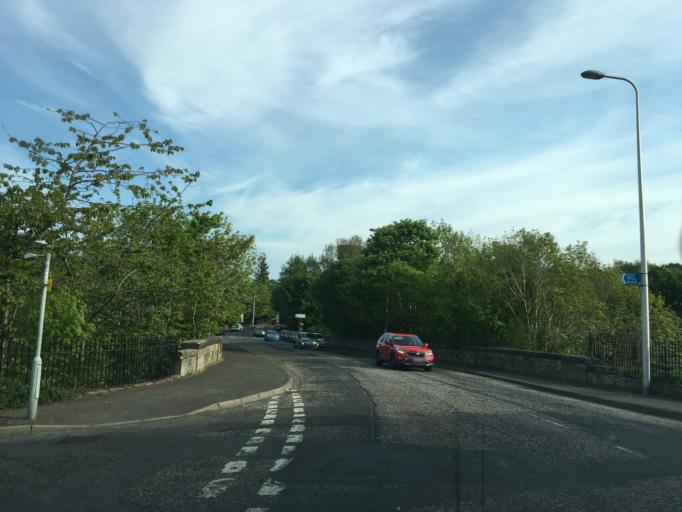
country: GB
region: Scotland
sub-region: Midlothian
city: Penicuik
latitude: 55.8240
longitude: -3.2217
